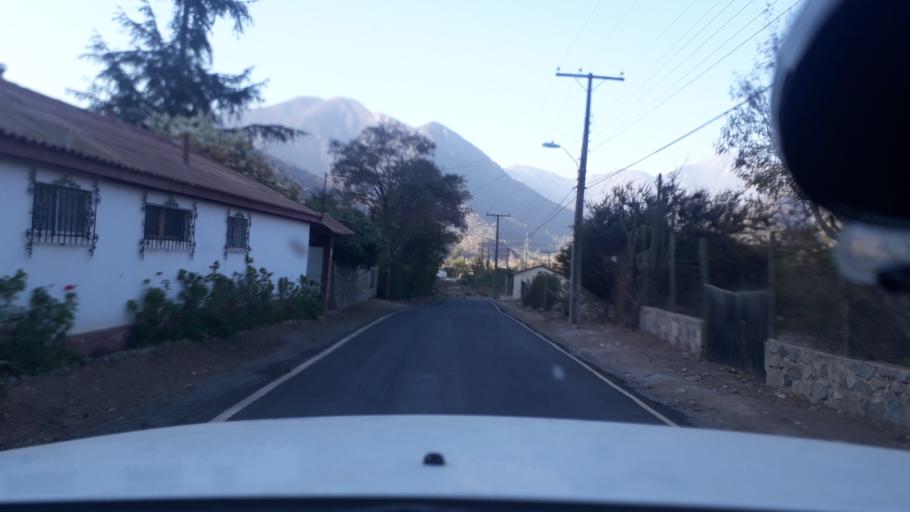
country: CL
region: Valparaiso
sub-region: Provincia de Marga Marga
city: Limache
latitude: -33.0563
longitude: -71.1132
